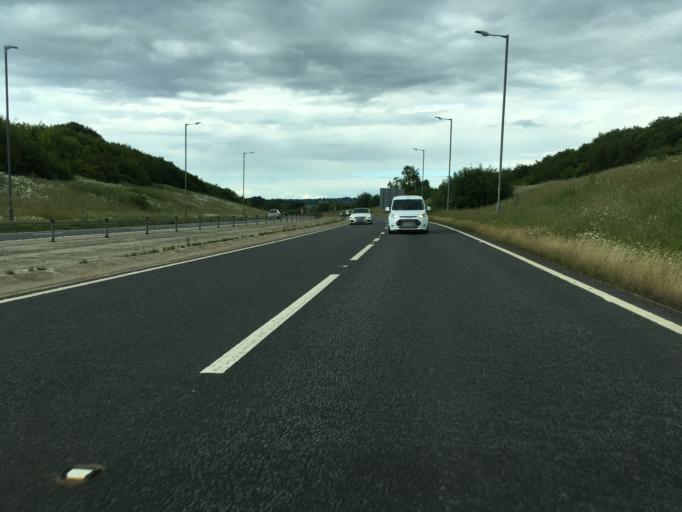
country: GB
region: England
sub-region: Central Bedfordshire
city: Leighton Buzzard
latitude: 51.9282
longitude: -0.6966
